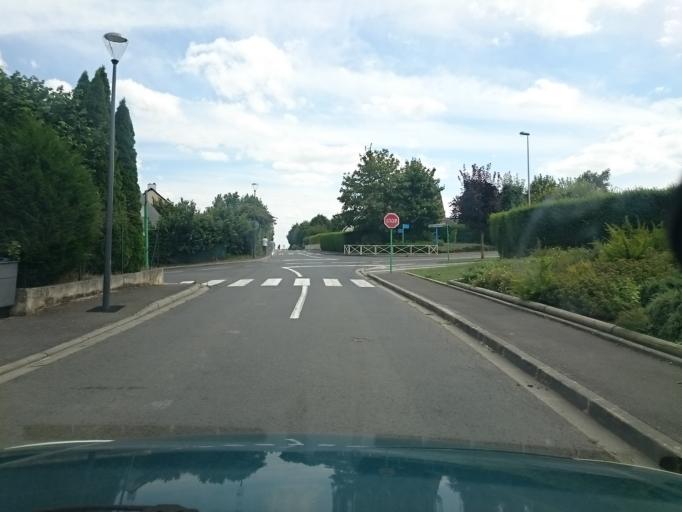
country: FR
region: Lower Normandy
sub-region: Departement du Calvados
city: Ifs
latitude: 49.1377
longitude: -0.3461
